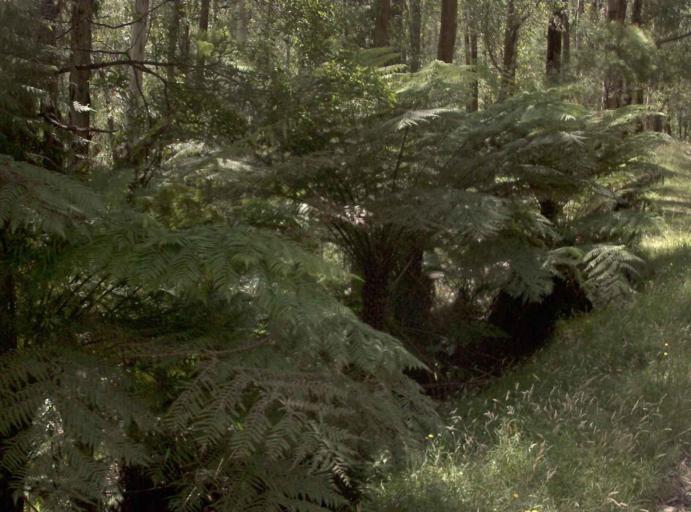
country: AU
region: Victoria
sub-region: Baw Baw
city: Warragul
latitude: -37.8953
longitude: 146.0280
